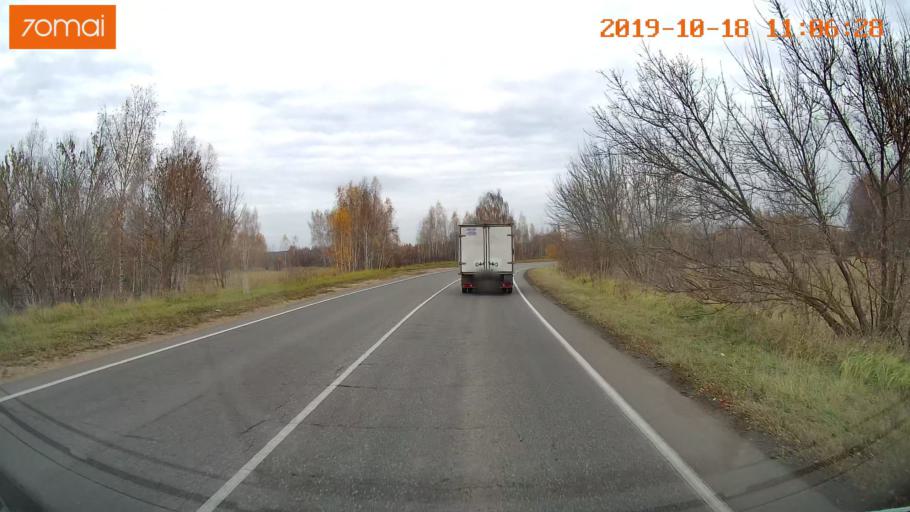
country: RU
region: Tula
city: Kimovsk
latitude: 53.9182
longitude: 38.5357
